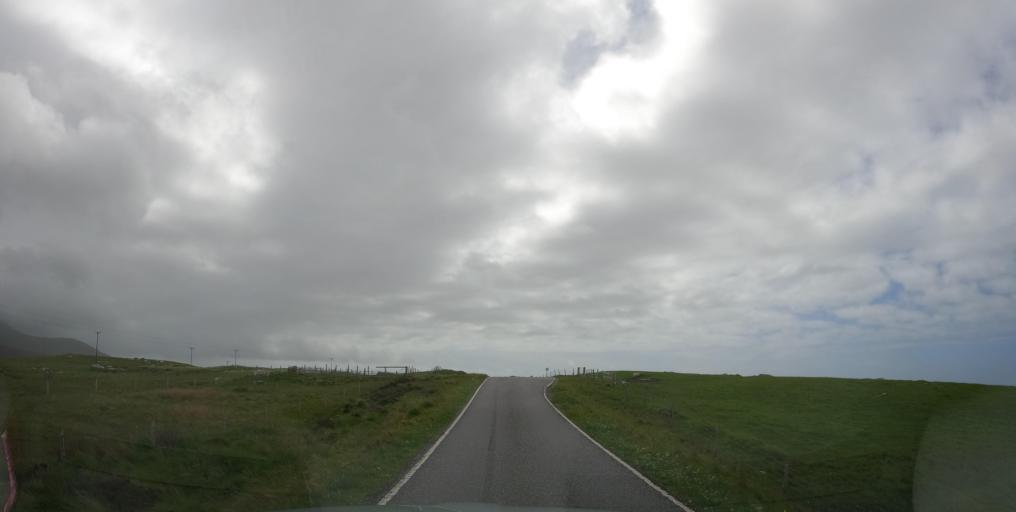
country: GB
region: Scotland
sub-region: Eilean Siar
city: Isle of South Uist
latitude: 57.2916
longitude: -7.3664
